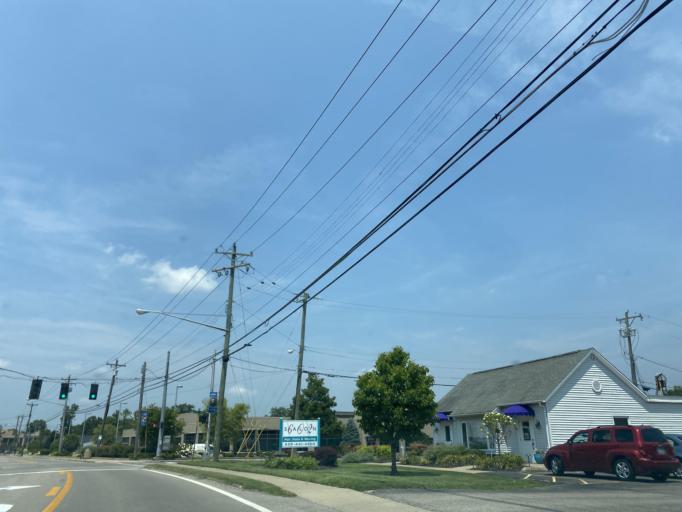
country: US
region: Kentucky
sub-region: Campbell County
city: Highland Heights
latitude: 39.0524
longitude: -84.4475
